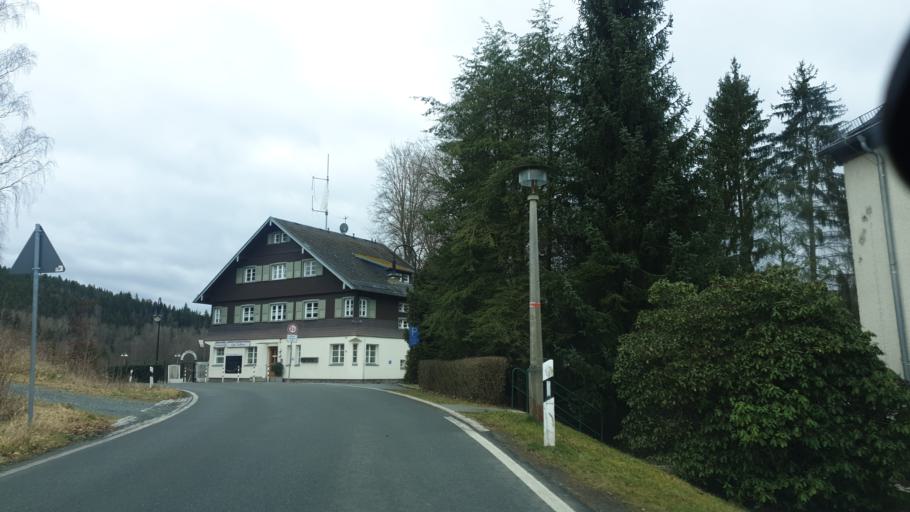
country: DE
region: Saxony
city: Bad Elster
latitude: 50.2726
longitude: 12.2485
